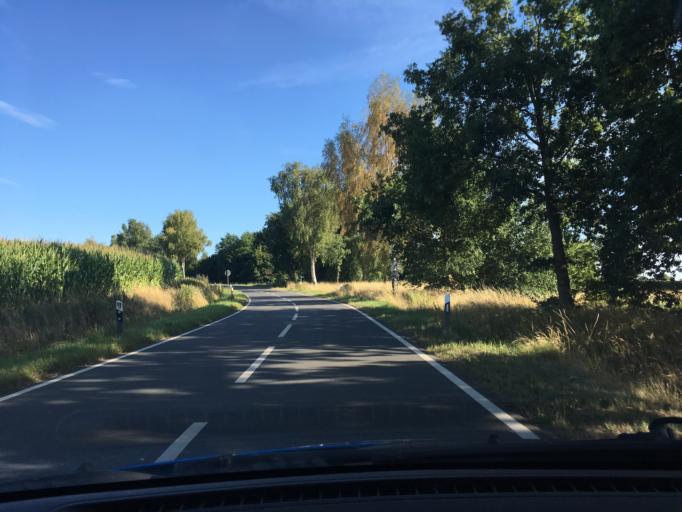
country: DE
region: Lower Saxony
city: Dahlenburg
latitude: 53.1932
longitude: 10.7205
